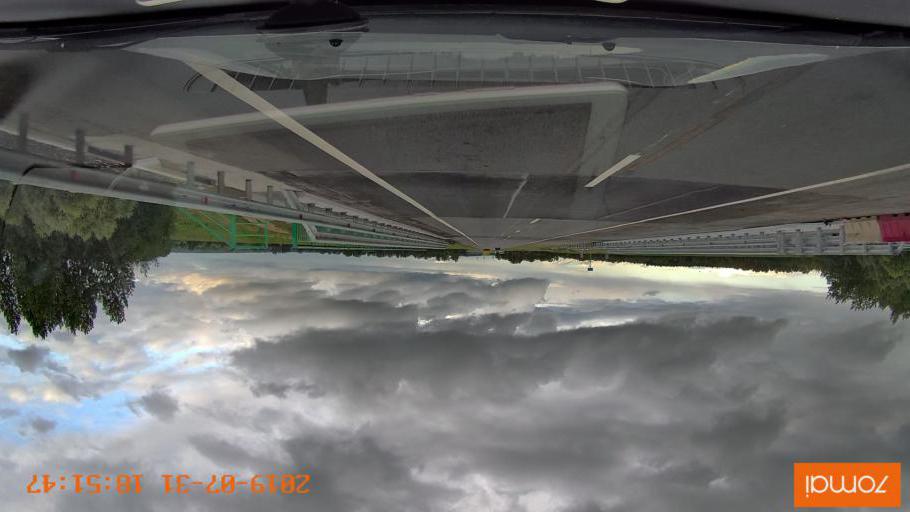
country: RU
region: Moskovskaya
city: Voskresensk
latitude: 55.2192
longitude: 38.6155
